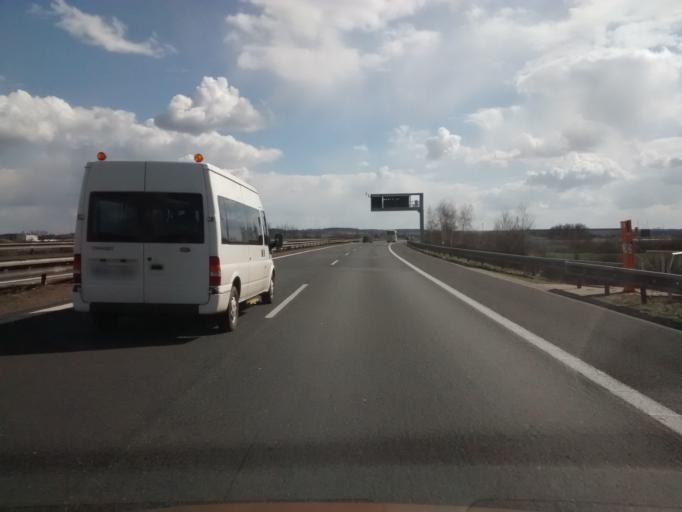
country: CZ
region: Central Bohemia
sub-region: Okres Melnik
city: Veltrusy
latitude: 50.2622
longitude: 14.3683
